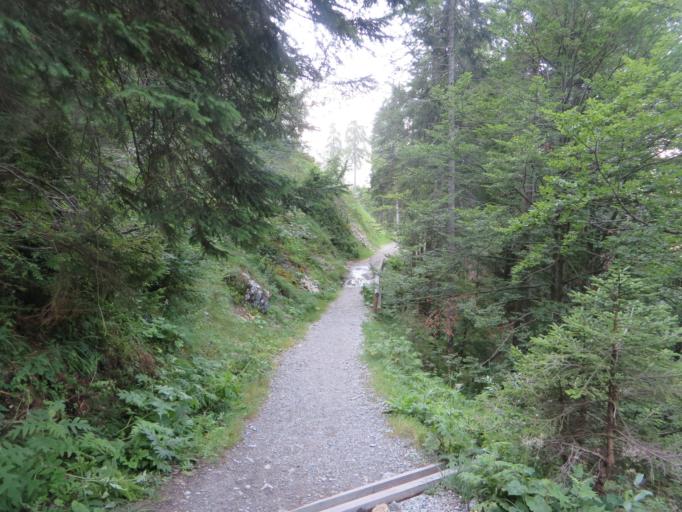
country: IT
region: Trentino-Alto Adige
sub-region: Provincia di Trento
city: Carisolo
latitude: 46.2132
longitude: 10.8273
